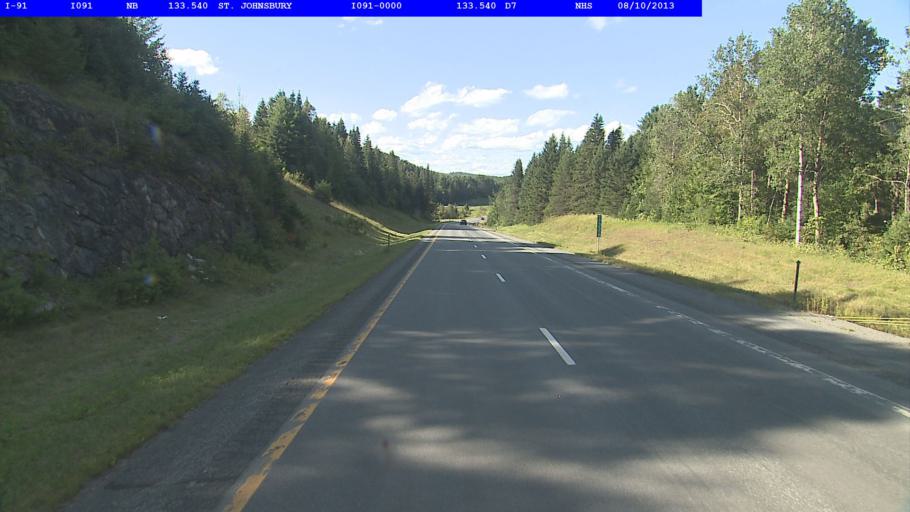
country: US
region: Vermont
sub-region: Caledonia County
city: St Johnsbury
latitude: 44.4680
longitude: -72.0240
